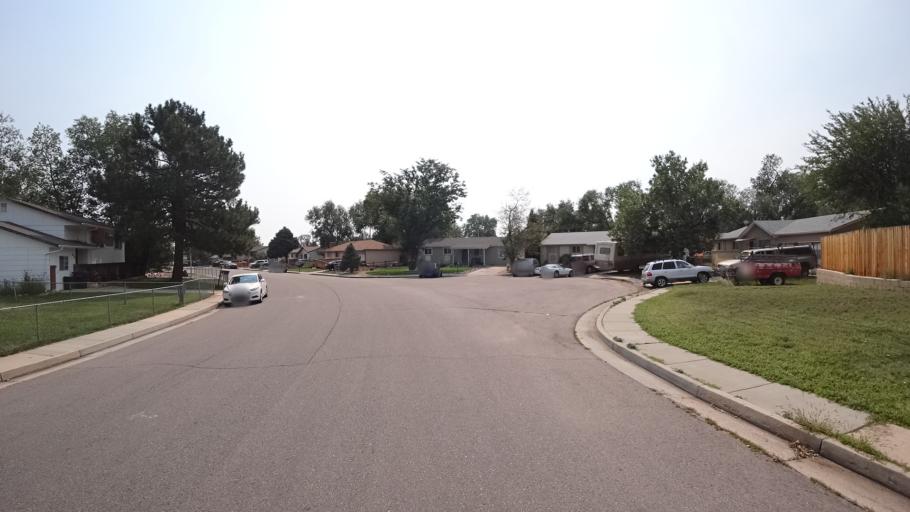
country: US
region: Colorado
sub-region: El Paso County
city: Colorado Springs
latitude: 38.8011
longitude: -104.8134
